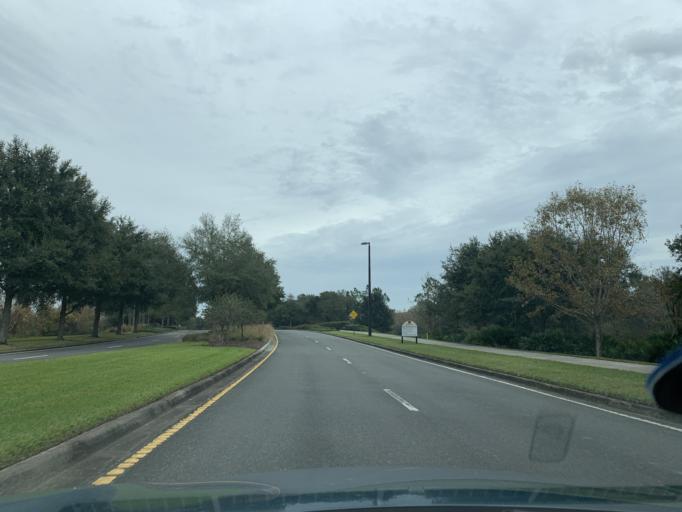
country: US
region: Florida
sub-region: Pasco County
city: Land O' Lakes
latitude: 28.2889
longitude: -82.4853
